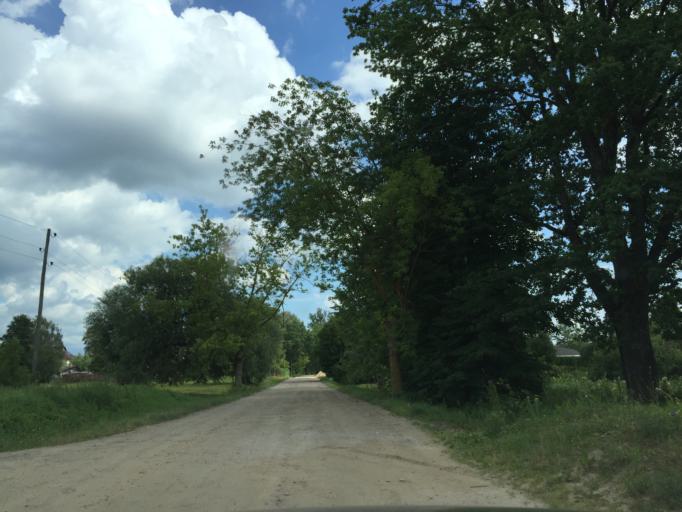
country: LV
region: Jelgava
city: Jelgava
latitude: 56.6461
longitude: 23.6875
